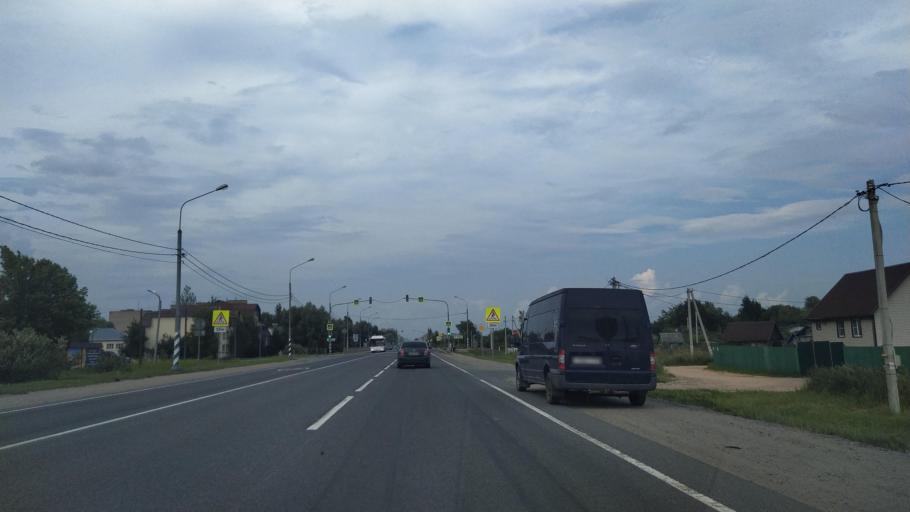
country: RU
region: Novgorod
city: Pankovka
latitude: 58.4946
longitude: 31.2092
